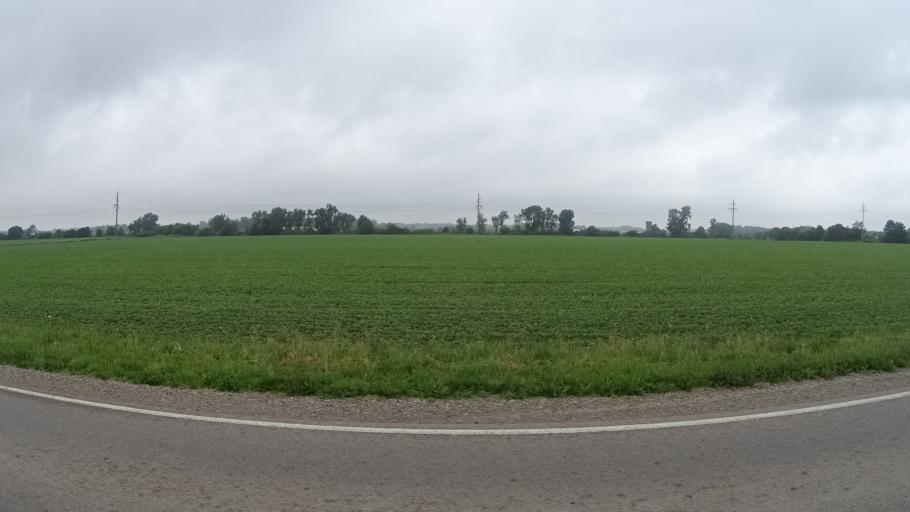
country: US
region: Ohio
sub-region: Huron County
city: Bellevue
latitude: 41.3420
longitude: -82.7975
